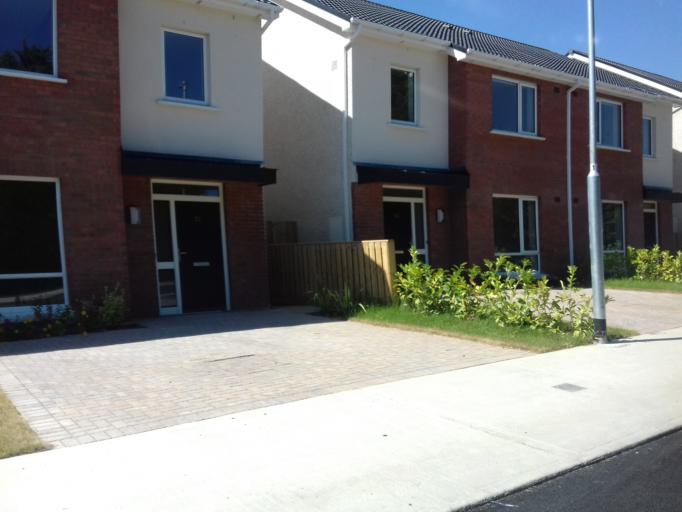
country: IE
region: Leinster
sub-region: Fingal County
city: Swords
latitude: 53.4512
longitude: -6.2512
